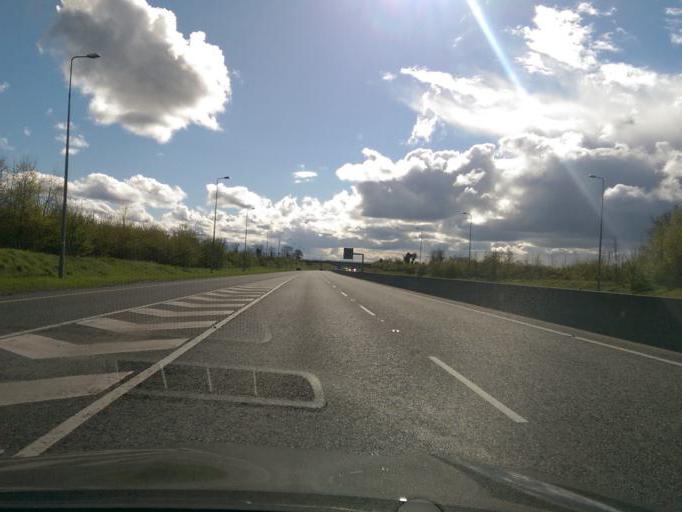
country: IE
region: Leinster
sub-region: An Iarmhi
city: Rochfortbridge
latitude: 53.4038
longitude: -7.2878
